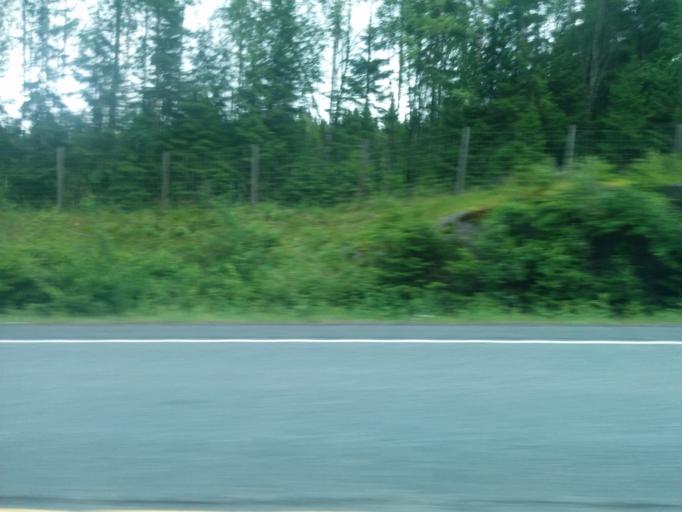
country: FI
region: Pirkanmaa
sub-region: Tampere
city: Orivesi
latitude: 61.6595
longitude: 24.2563
